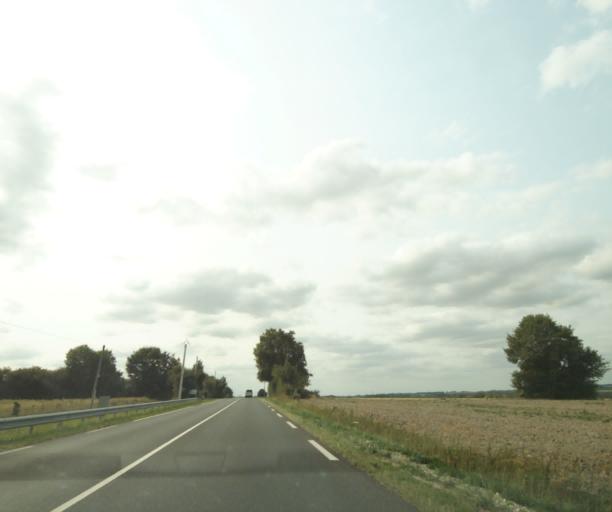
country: FR
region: Centre
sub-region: Departement de l'Indre
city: Clion
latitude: 46.9224
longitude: 1.2969
